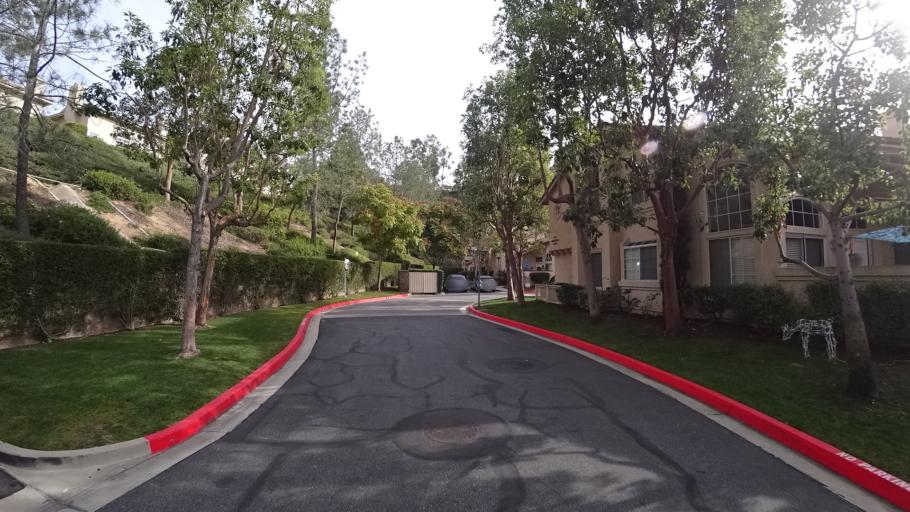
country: US
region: California
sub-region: Orange County
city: Laguna Woods
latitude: 33.6055
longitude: -117.7403
